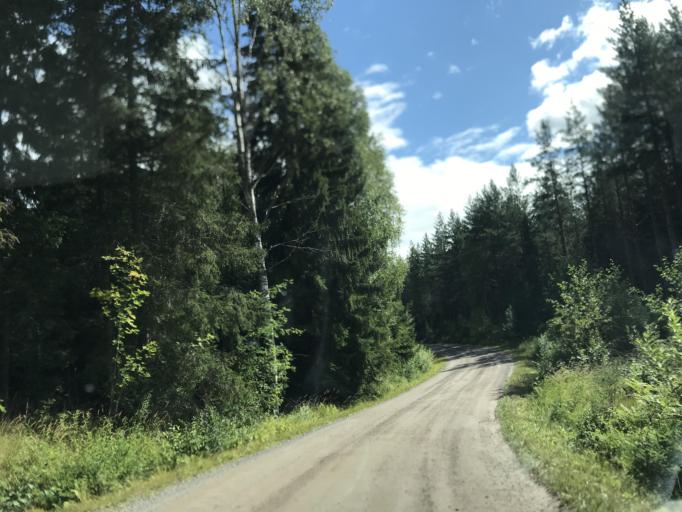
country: FI
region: Uusimaa
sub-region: Helsinki
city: Kaerkoelae
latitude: 60.6388
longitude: 23.8215
